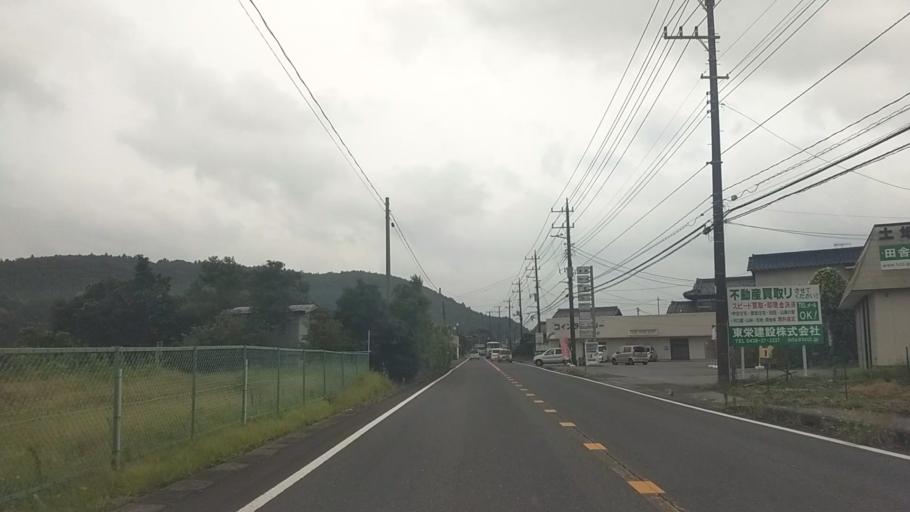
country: JP
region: Chiba
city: Kisarazu
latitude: 35.3083
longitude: 140.0670
